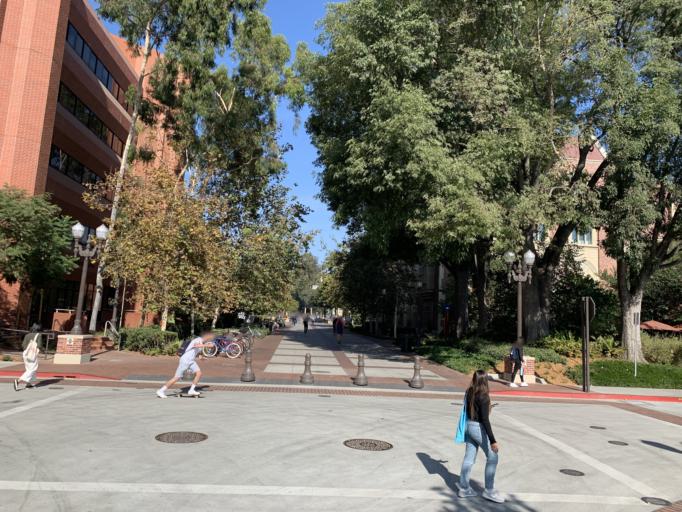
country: US
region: California
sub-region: Los Angeles County
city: Los Angeles
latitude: 34.0203
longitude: -118.2878
